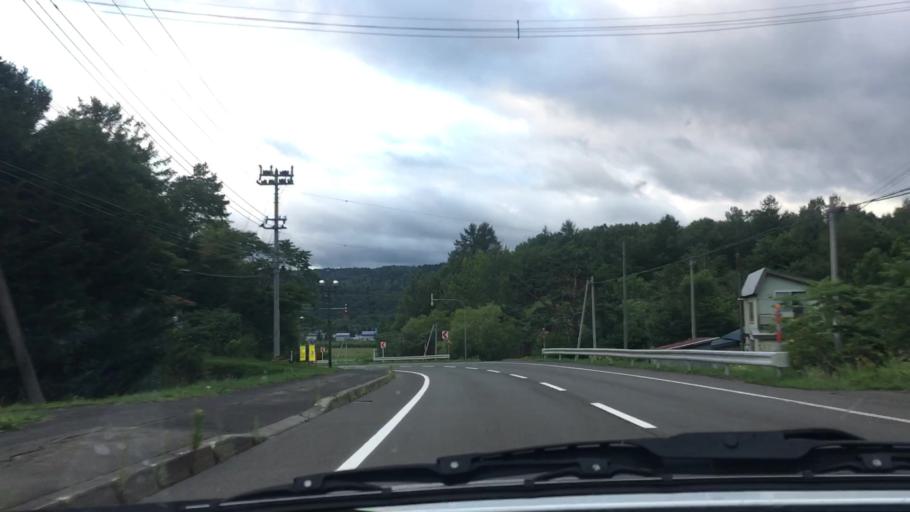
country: JP
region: Hokkaido
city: Shimo-furano
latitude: 42.9882
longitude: 142.3987
